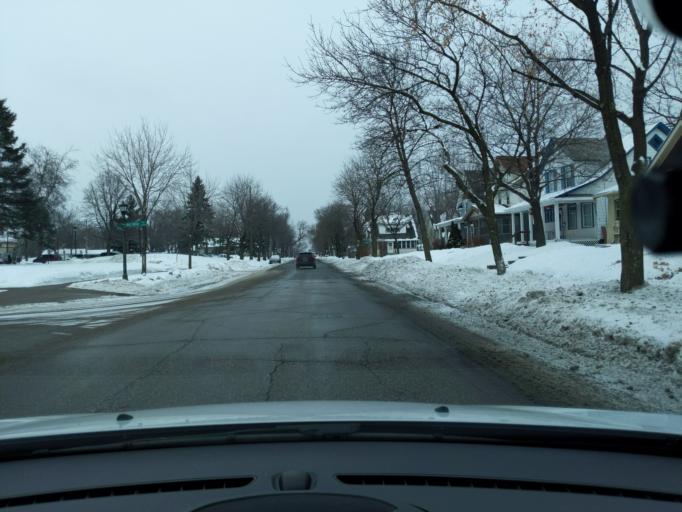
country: US
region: Minnesota
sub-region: Ramsey County
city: Falcon Heights
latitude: 44.9640
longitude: -93.1569
